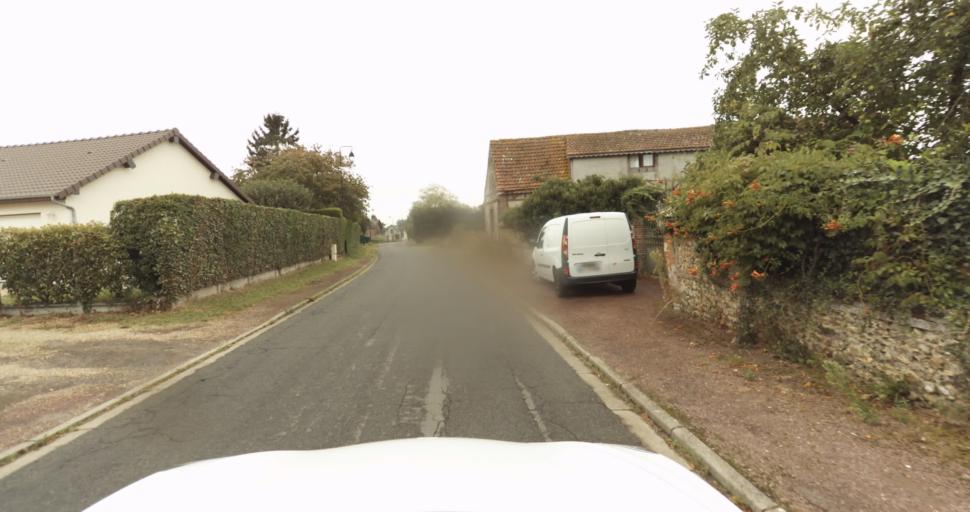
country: FR
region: Haute-Normandie
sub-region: Departement de l'Eure
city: Aviron
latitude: 49.0769
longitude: 1.0880
